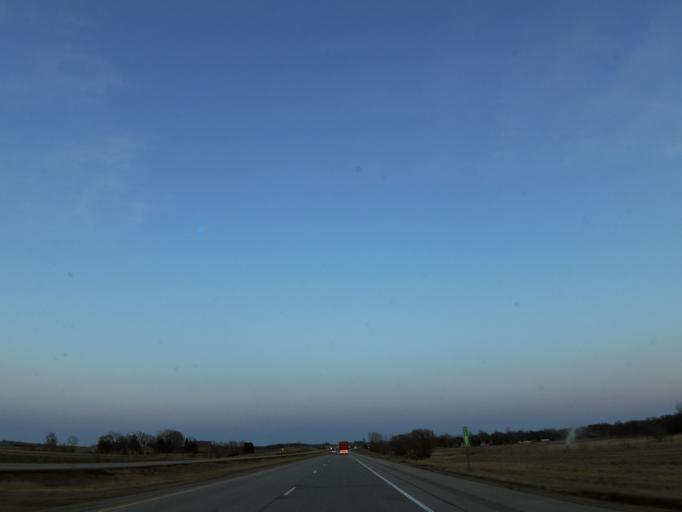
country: US
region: Minnesota
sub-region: Mower County
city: Austin
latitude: 43.6736
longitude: -92.8071
